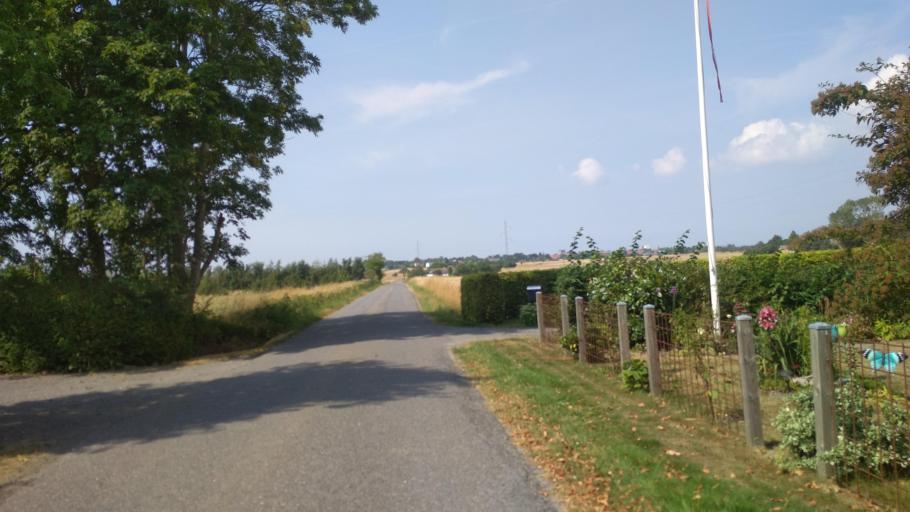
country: DK
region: Capital Region
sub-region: Bornholm Kommune
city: Akirkeby
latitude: 55.0616
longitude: 14.9473
